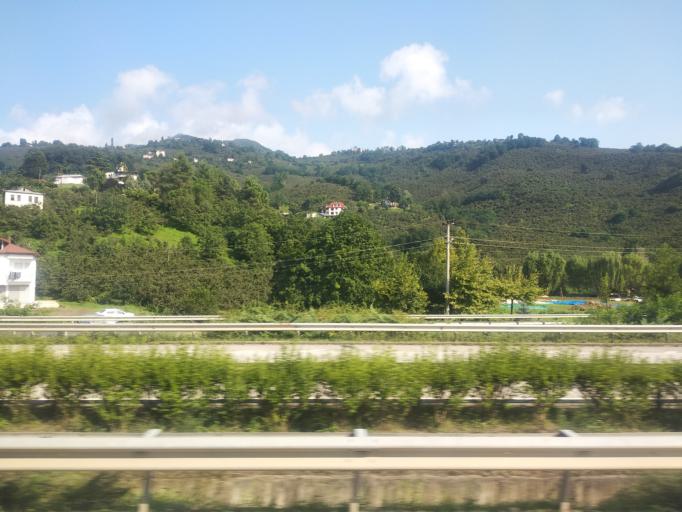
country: TR
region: Ordu
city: Ordu
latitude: 41.0076
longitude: 37.8296
